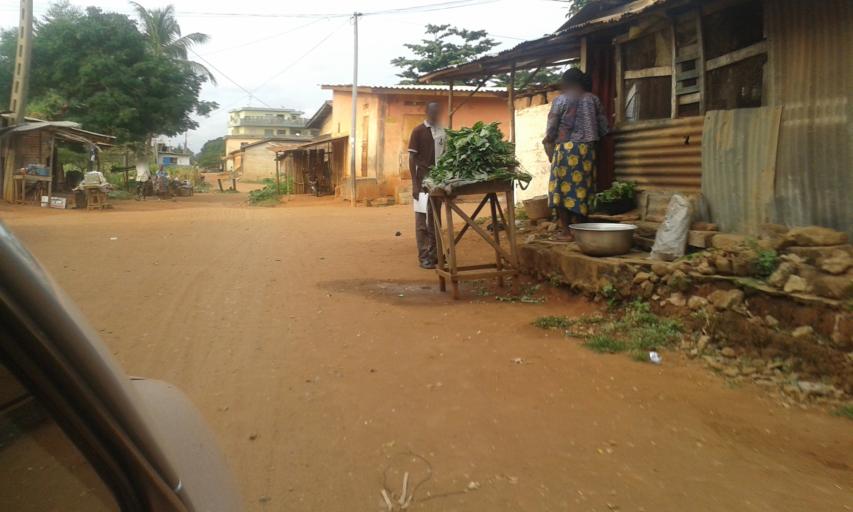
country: BJ
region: Queme
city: Porto-Novo
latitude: 6.4780
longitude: 2.6104
